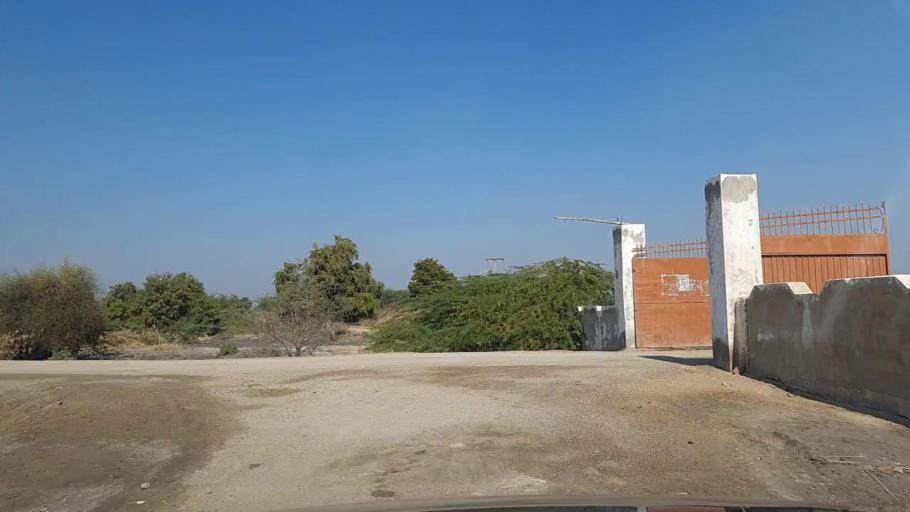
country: PK
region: Sindh
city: Nawabshah
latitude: 26.3197
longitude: 68.3501
